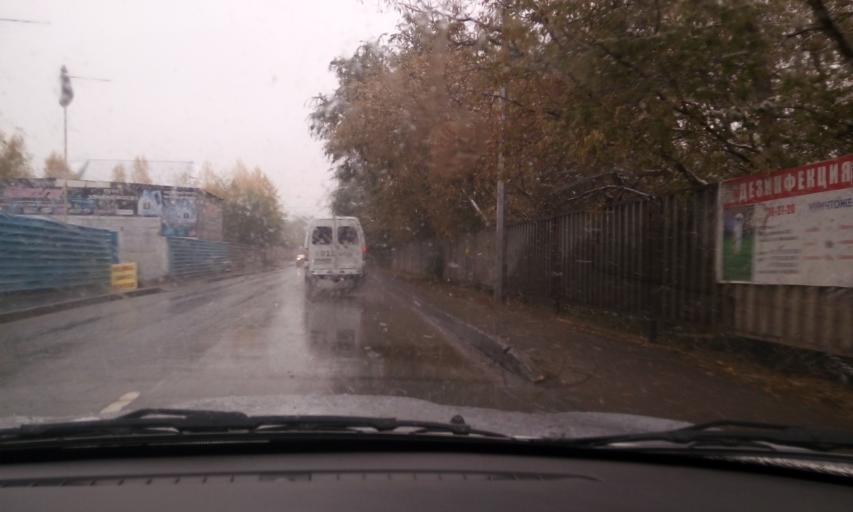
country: KZ
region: Astana Qalasy
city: Astana
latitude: 51.1418
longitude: 71.4320
